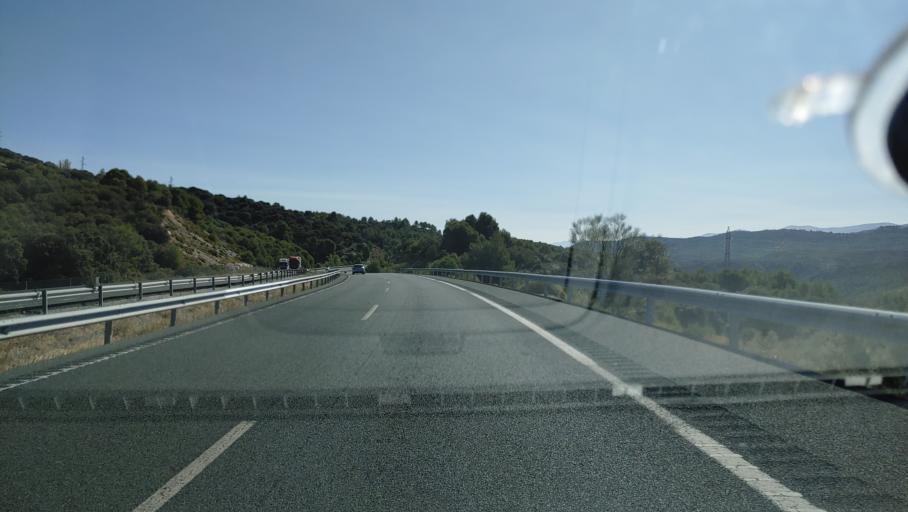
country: ES
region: Andalusia
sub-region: Provincia de Granada
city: Diezma
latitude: 37.3108
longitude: -3.3802
